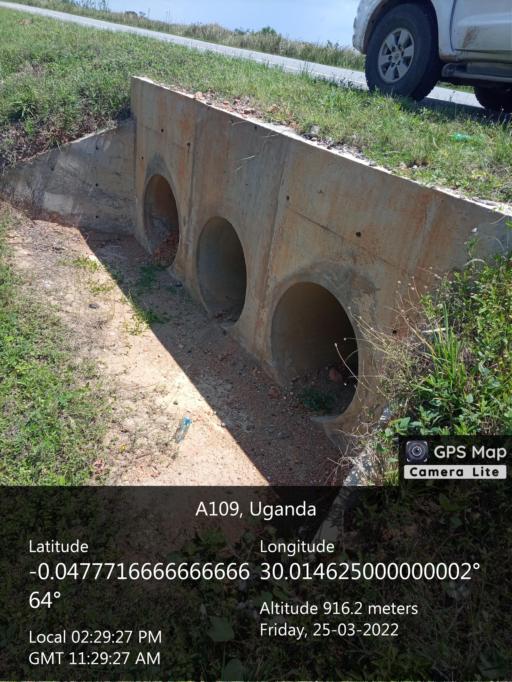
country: UG
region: Western Region
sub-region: Kasese District
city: Kasese
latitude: -0.0478
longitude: 30.0146
